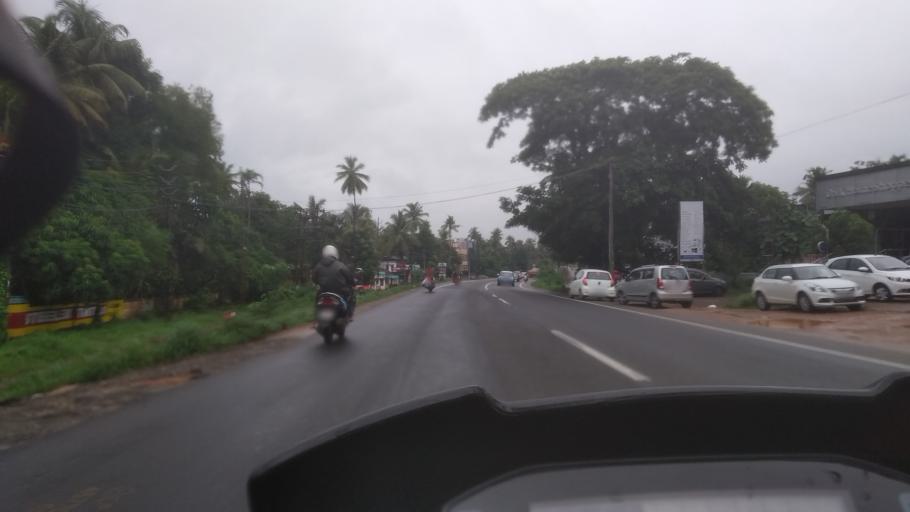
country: IN
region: Kerala
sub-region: Alappuzha
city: Kayankulam
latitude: 9.1625
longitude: 76.5048
